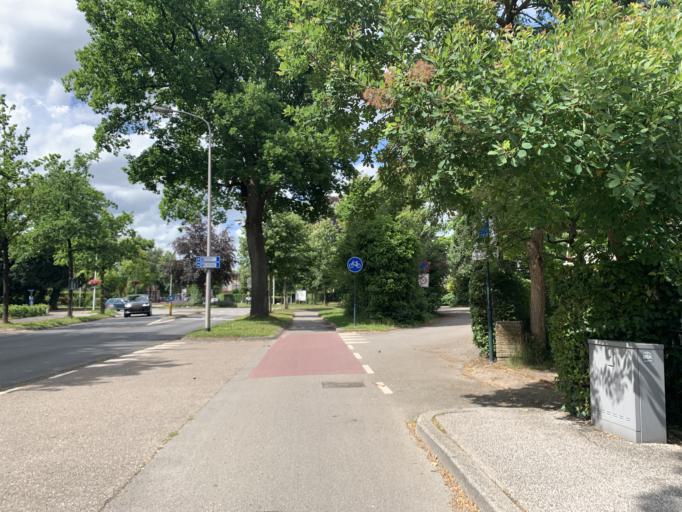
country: NL
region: Groningen
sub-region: Gemeente Haren
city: Haren
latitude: 53.1698
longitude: 6.6072
